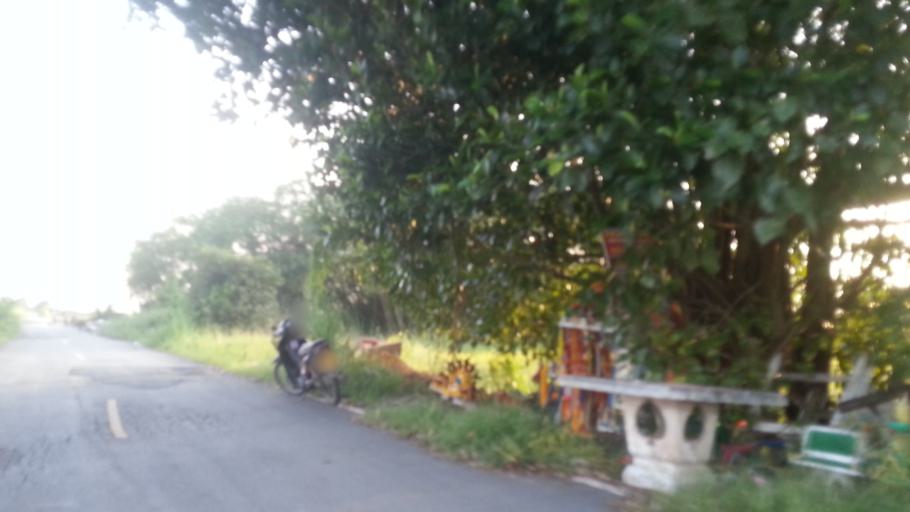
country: TH
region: Pathum Thani
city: Nong Suea
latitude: 14.0421
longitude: 100.8570
